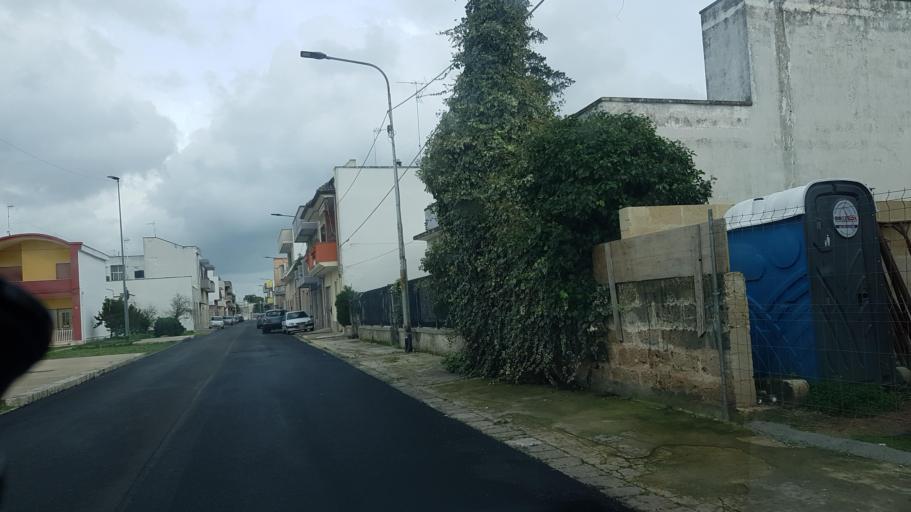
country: IT
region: Apulia
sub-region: Provincia di Lecce
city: Carmiano
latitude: 40.3401
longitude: 18.0455
